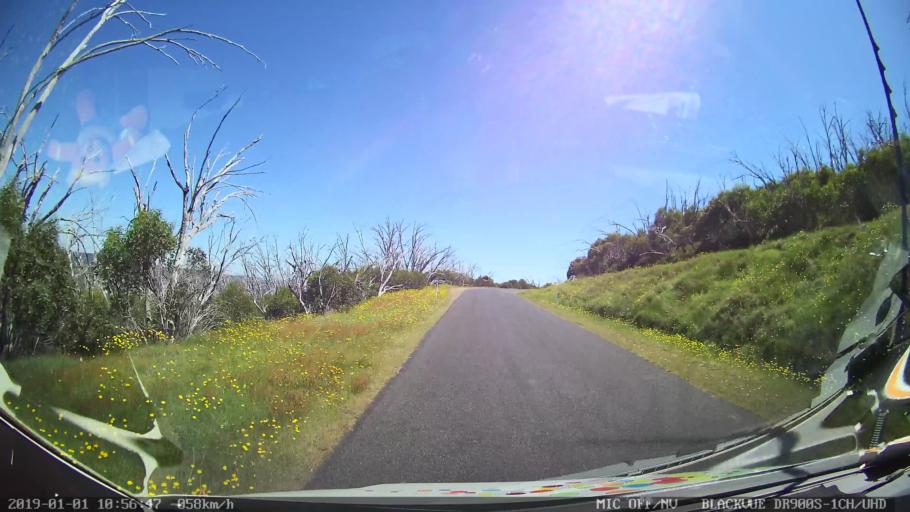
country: AU
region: New South Wales
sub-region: Snowy River
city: Jindabyne
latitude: -36.0019
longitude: 148.3941
